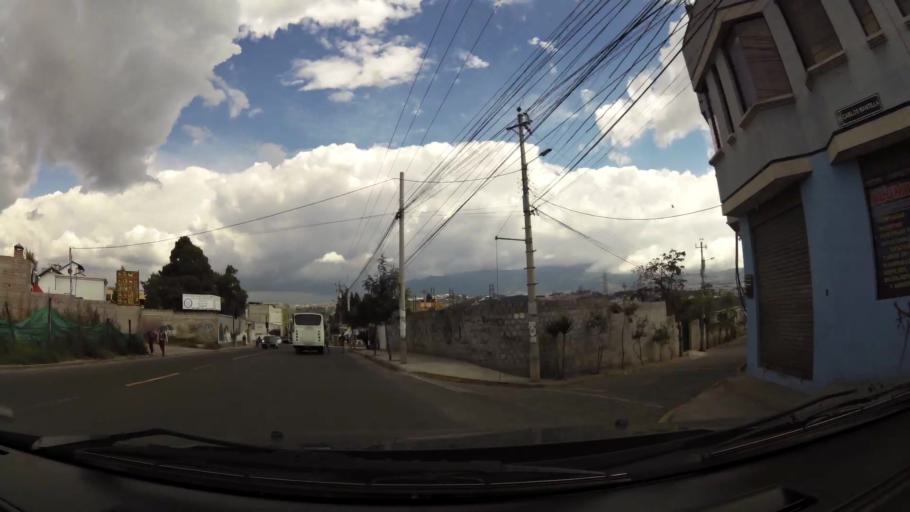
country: EC
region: Pichincha
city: Quito
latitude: -0.0862
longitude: -78.4379
